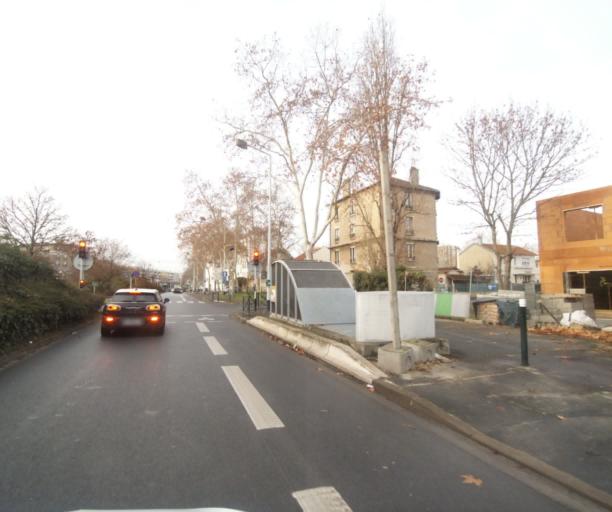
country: FR
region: Ile-de-France
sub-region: Departement des Hauts-de-Seine
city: Nanterre
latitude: 48.8977
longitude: 2.1973
